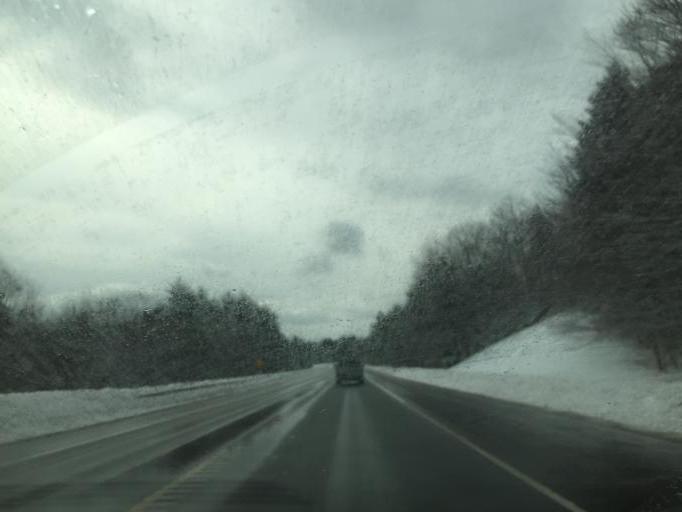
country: US
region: New Hampshire
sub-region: Carroll County
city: Sanbornville
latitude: 43.5066
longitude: -71.0292
